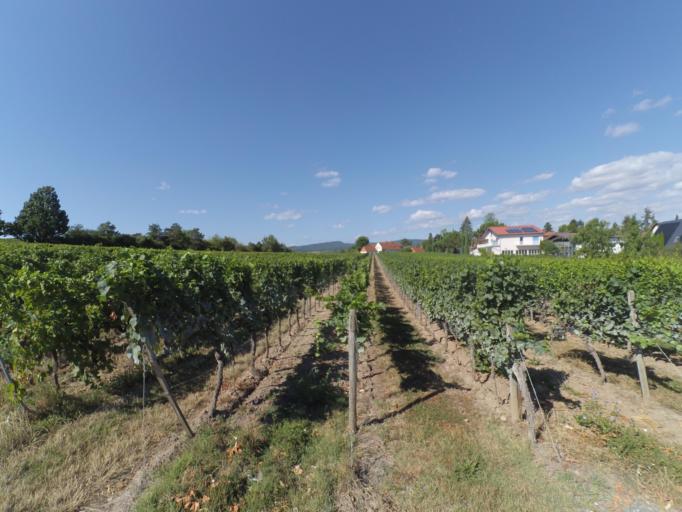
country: DE
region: Rheinland-Pfalz
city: Freinsheim
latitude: 49.5001
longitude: 8.2053
